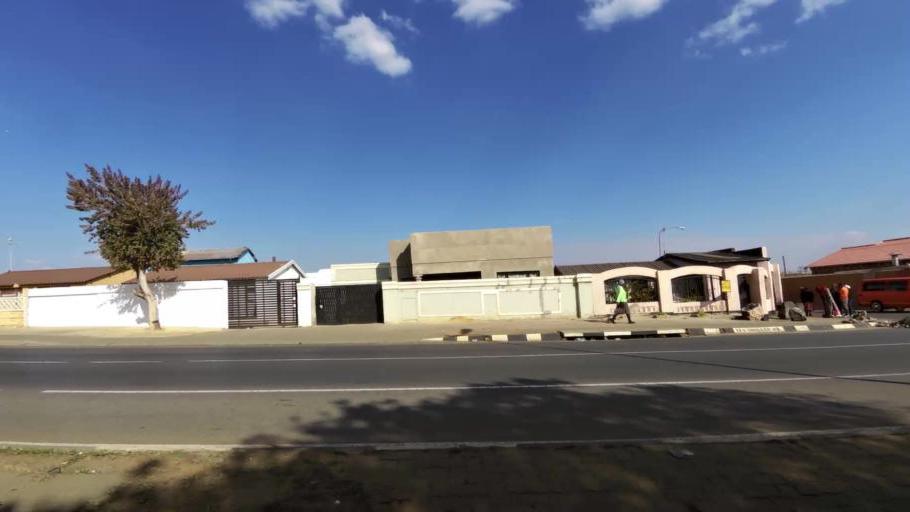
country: ZA
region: Gauteng
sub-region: City of Johannesburg Metropolitan Municipality
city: Roodepoort
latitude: -26.2143
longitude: 27.8782
